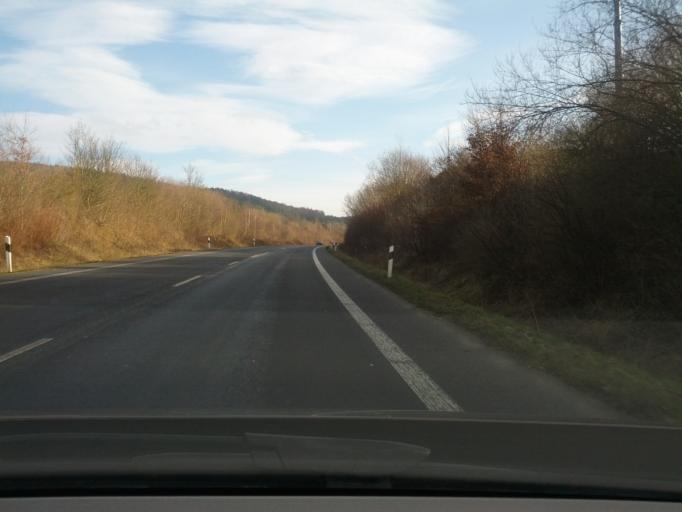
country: DE
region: Lower Saxony
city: Scheden
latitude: 51.3963
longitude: 9.7536
